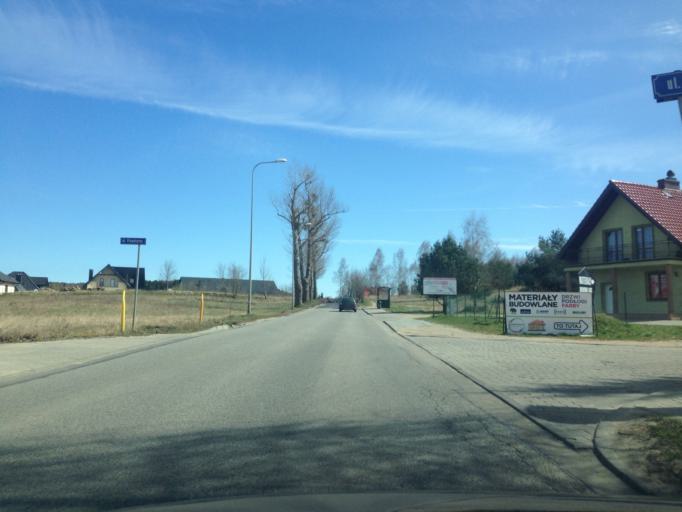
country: PL
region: Pomeranian Voivodeship
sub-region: Powiat kartuski
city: Chwaszczyno
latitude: 54.4860
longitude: 18.4327
